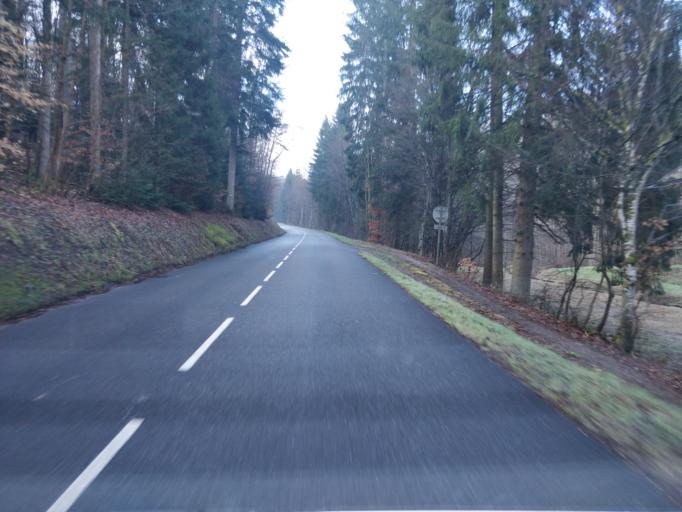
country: FR
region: Lorraine
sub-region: Departement de la Moselle
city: Soucht
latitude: 48.9206
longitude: 7.2918
